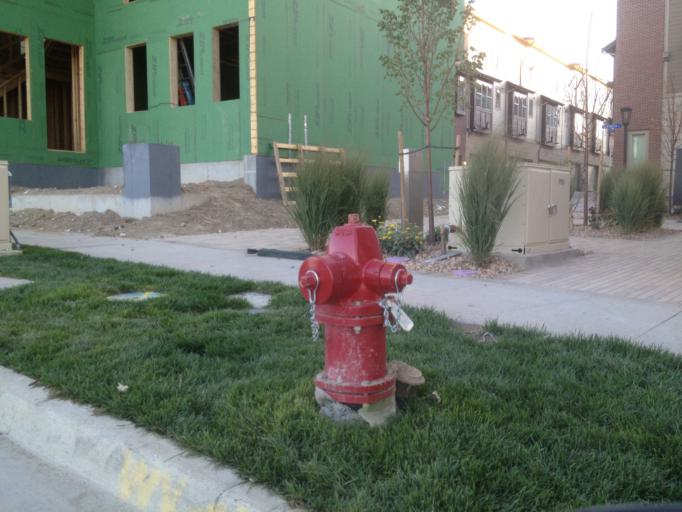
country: US
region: Colorado
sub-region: Boulder County
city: Superior
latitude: 39.9507
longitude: -105.1592
